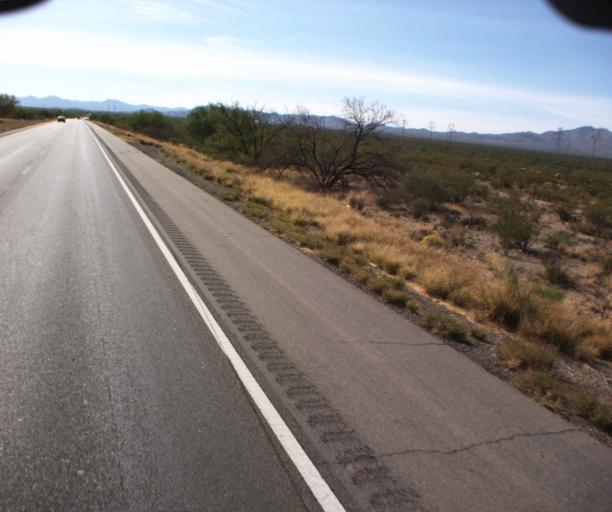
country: US
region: Arizona
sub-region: Pima County
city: Vail
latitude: 32.0479
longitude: -110.7521
